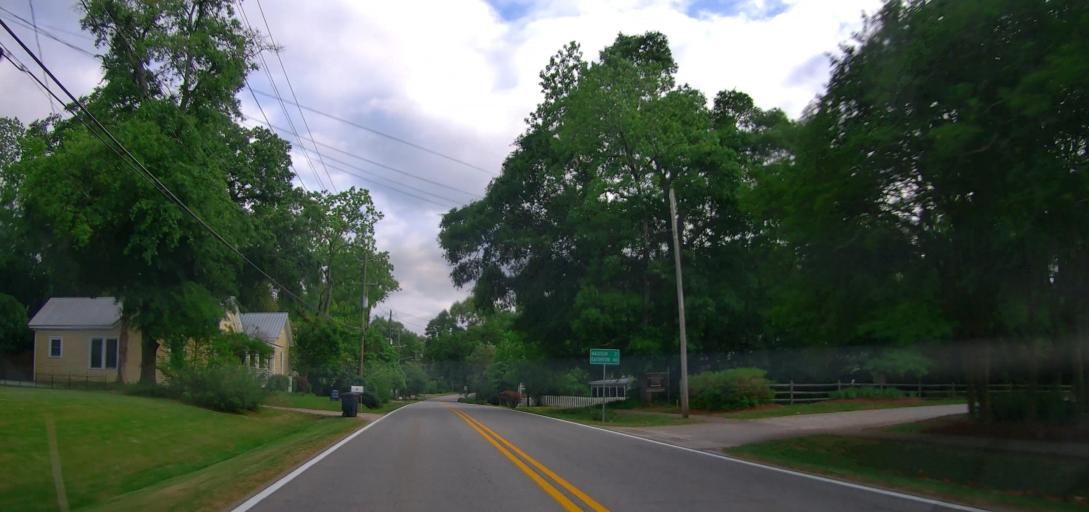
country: US
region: Georgia
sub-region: Oconee County
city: Watkinsville
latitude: 33.8586
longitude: -83.4072
